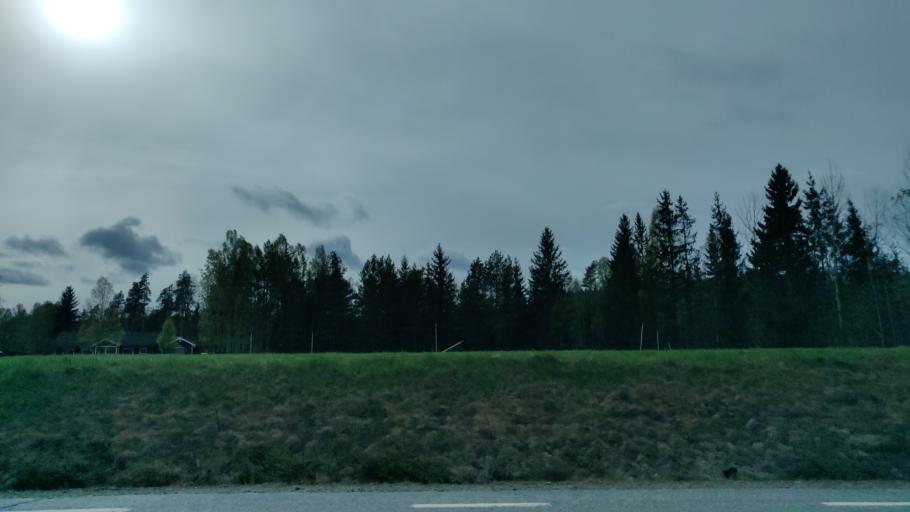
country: SE
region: Vaermland
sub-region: Munkfors Kommun
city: Munkfors
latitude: 59.8046
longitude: 13.5053
